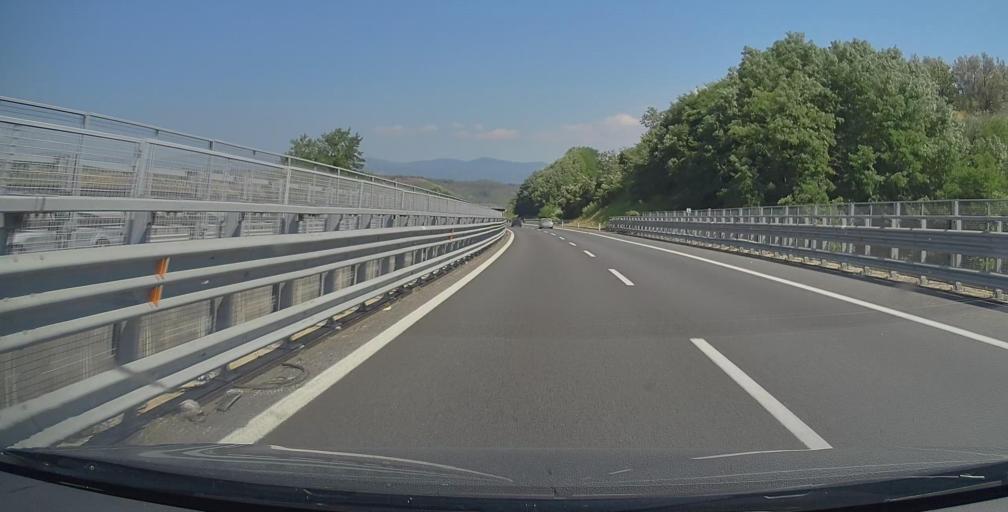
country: IT
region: Calabria
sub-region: Provincia di Vibo-Valentia
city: Sant'Onofrio
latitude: 38.6839
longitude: 16.1649
